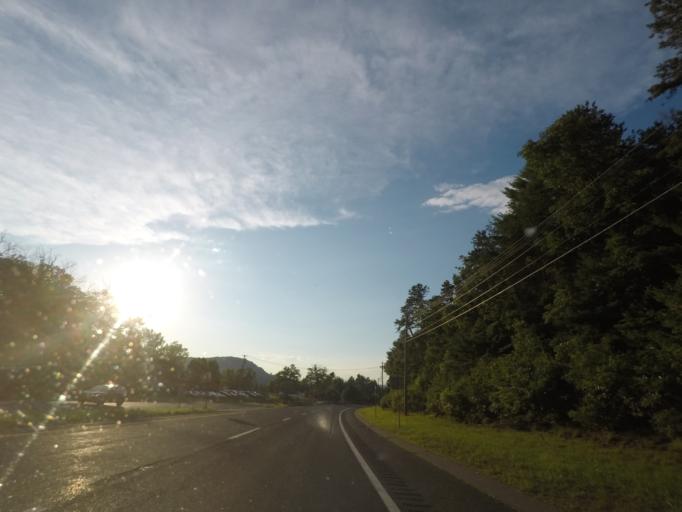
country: US
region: Massachusetts
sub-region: Hampden County
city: Brimfield
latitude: 42.1210
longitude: -72.2491
